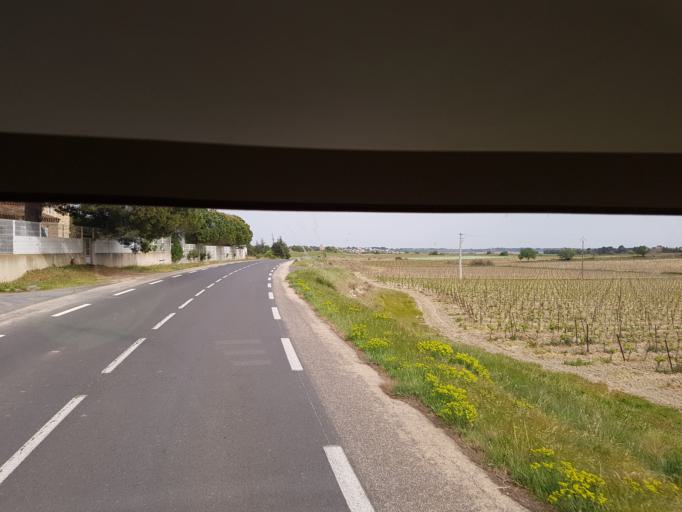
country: FR
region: Languedoc-Roussillon
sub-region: Departement de l'Herault
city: Vendres
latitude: 43.2758
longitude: 3.1990
